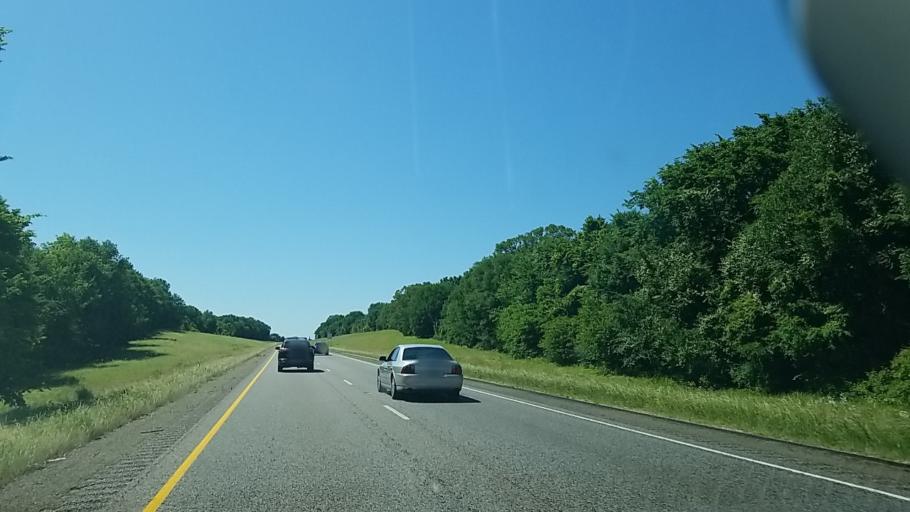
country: US
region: Texas
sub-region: Freestone County
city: Fairfield
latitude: 31.8114
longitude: -96.2698
